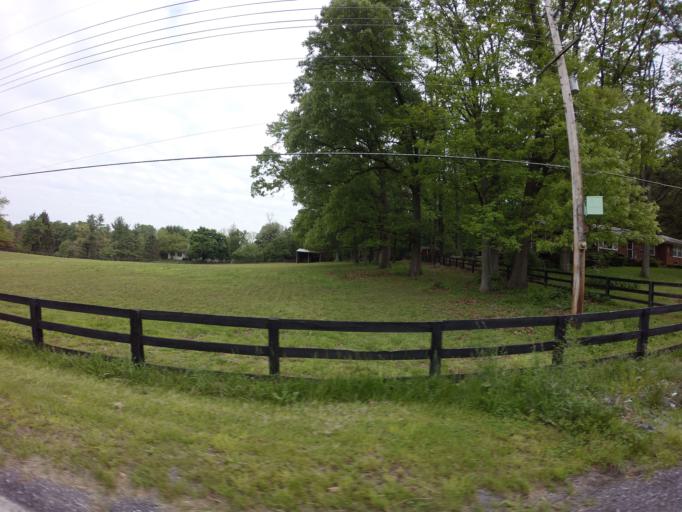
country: US
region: Maryland
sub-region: Frederick County
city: Green Valley
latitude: 39.2877
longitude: -77.2841
